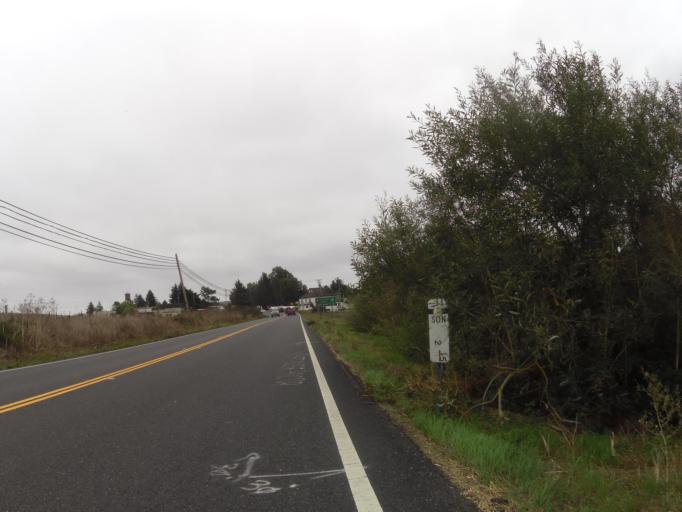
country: US
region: California
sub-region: Sonoma County
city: Occidental
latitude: 38.3192
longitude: -122.9272
